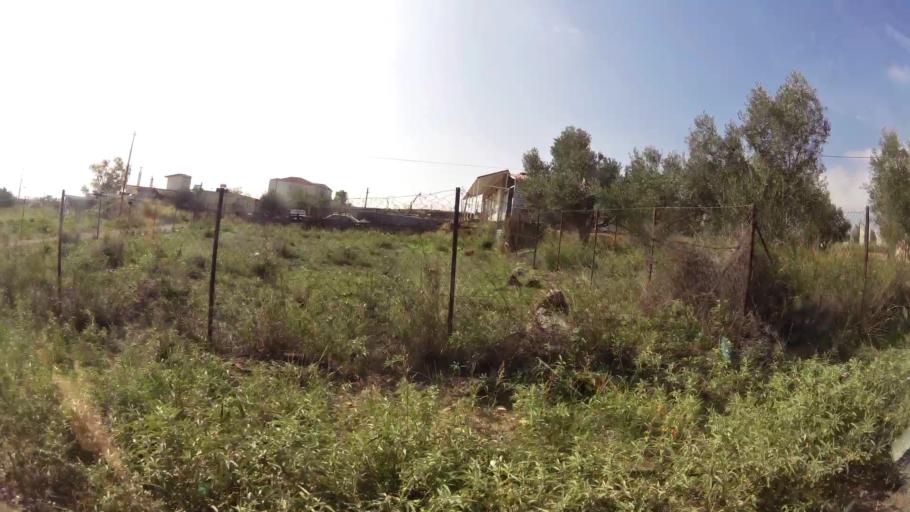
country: GR
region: Attica
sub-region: Nomarchia Dytikis Attikis
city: Zefyri
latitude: 38.0605
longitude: 23.7263
